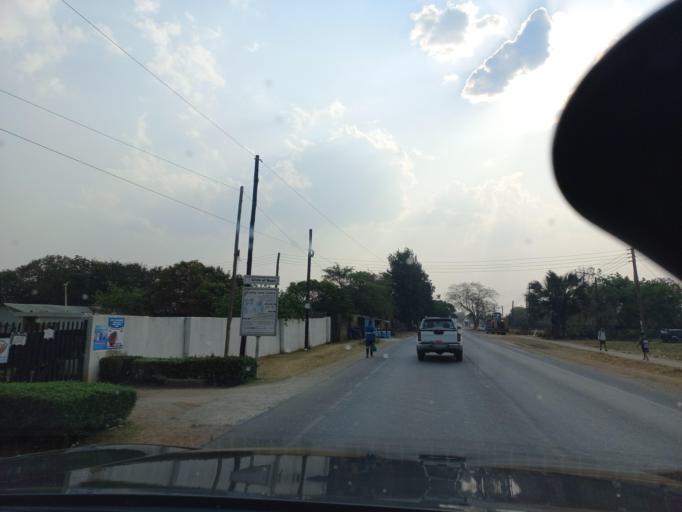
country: ZM
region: Lusaka
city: Lusaka
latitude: -15.4637
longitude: 28.2411
